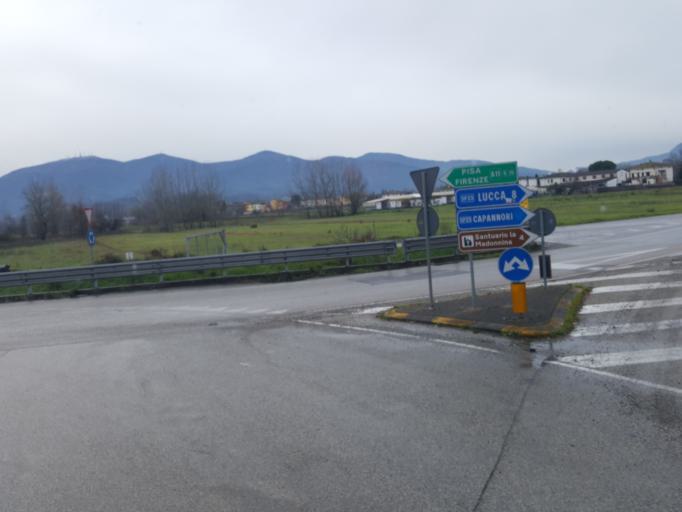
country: IT
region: Tuscany
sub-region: Provincia di Lucca
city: Porcari
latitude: 43.8414
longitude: 10.5952
